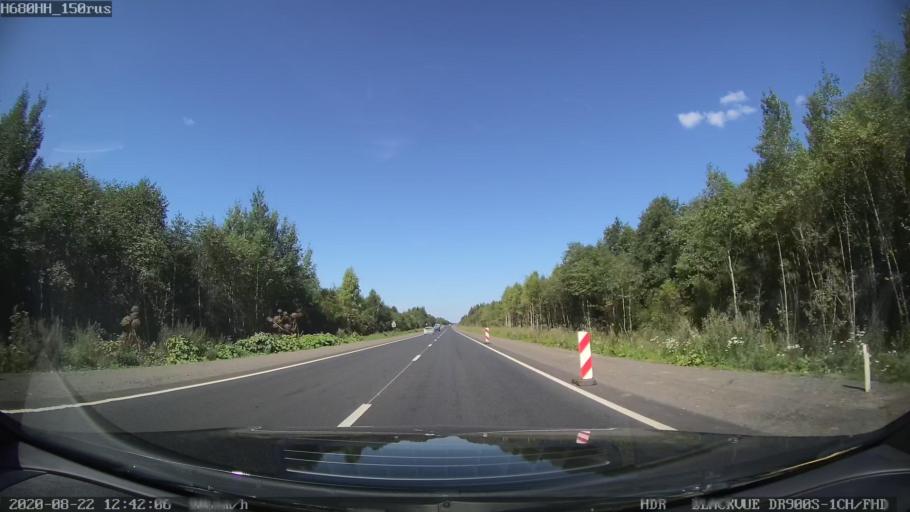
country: RU
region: Tverskaya
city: Rameshki
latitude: 57.3567
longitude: 36.0964
